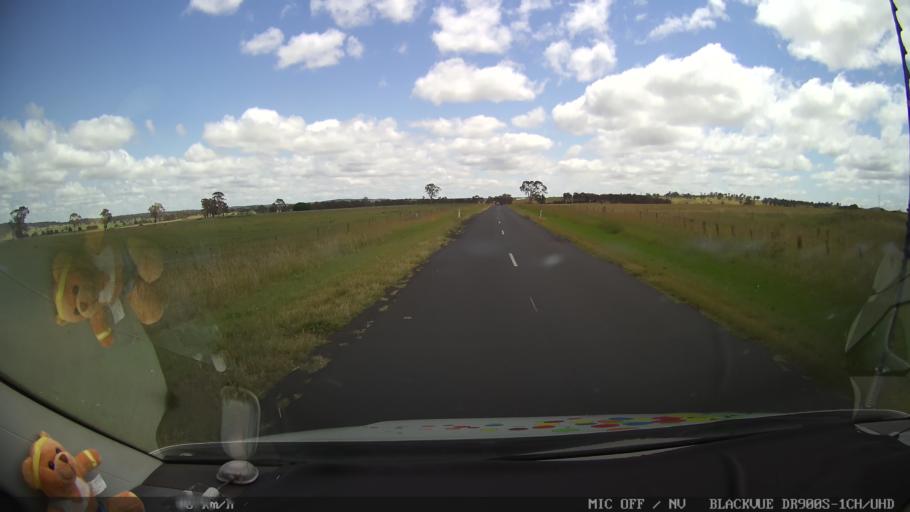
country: AU
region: New South Wales
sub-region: Glen Innes Severn
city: Glen Innes
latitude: -29.6595
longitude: 151.6925
